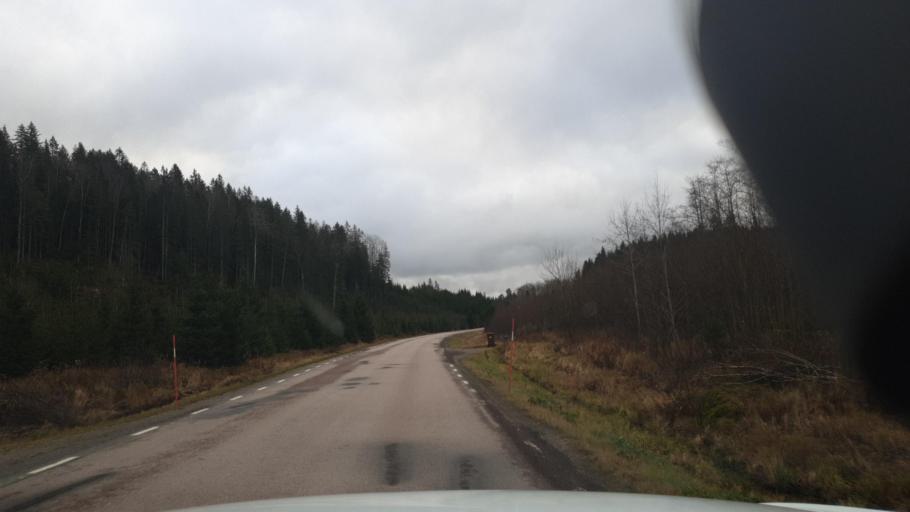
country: SE
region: Vaermland
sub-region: Arvika Kommun
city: Arvika
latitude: 59.6813
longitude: 12.7937
